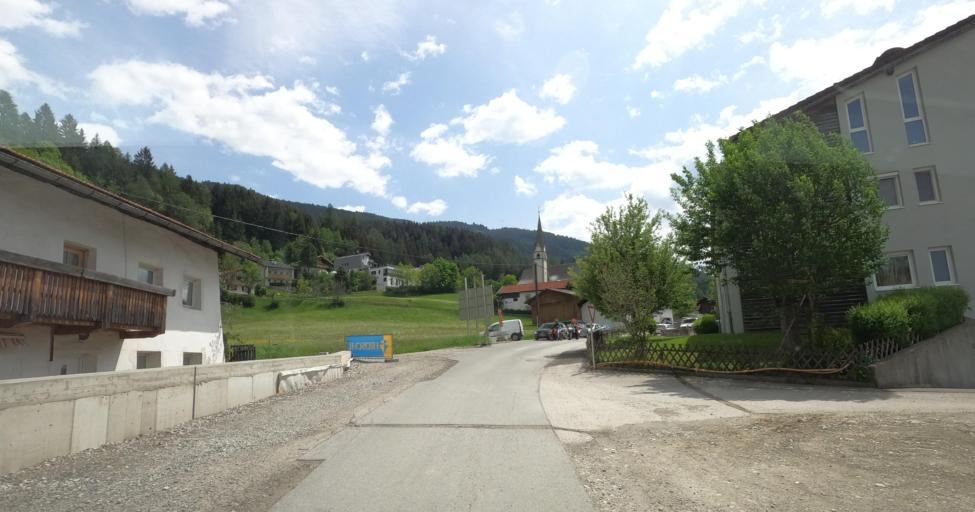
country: AT
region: Tyrol
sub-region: Politischer Bezirk Innsbruck Land
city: Pfons
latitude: 47.1430
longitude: 11.4603
